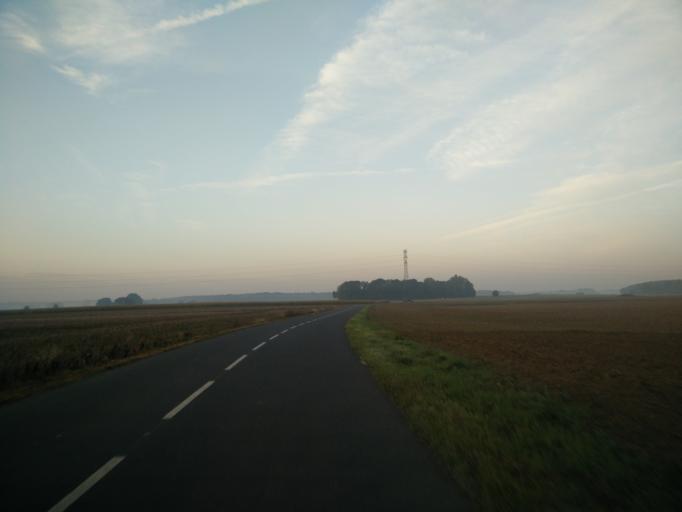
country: FR
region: Picardie
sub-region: Departement de l'Oise
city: Lassigny
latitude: 49.6528
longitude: 2.8956
